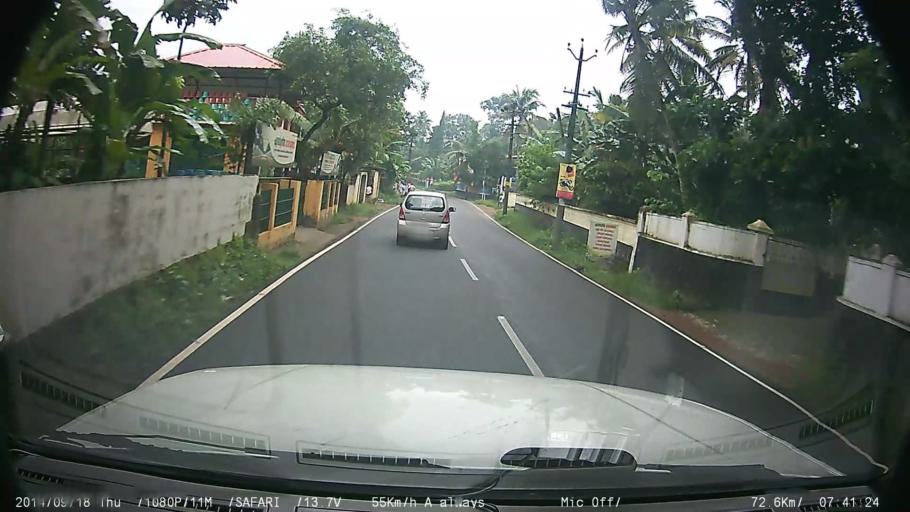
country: IN
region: Kerala
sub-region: Kottayam
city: Changanacheri
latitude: 9.4597
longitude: 76.5774
